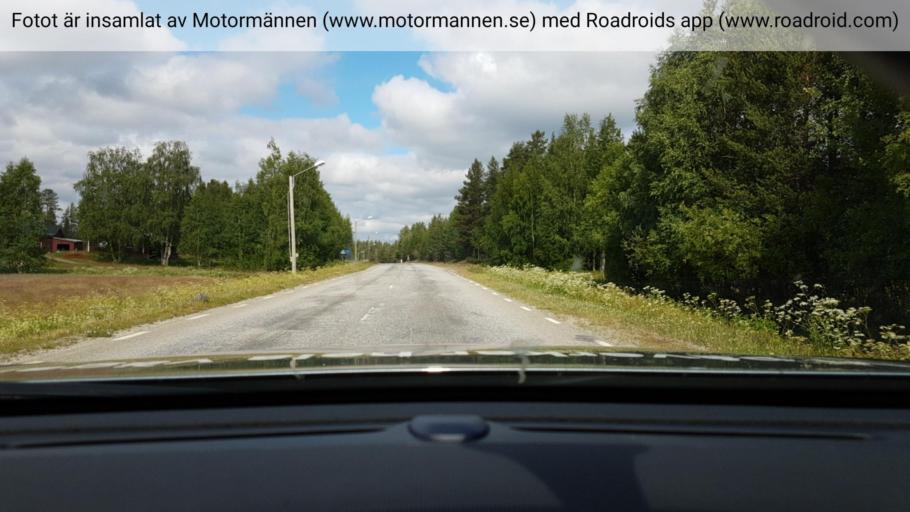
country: SE
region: Vaesterbotten
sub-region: Mala Kommun
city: Mala
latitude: 64.9069
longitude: 18.6801
